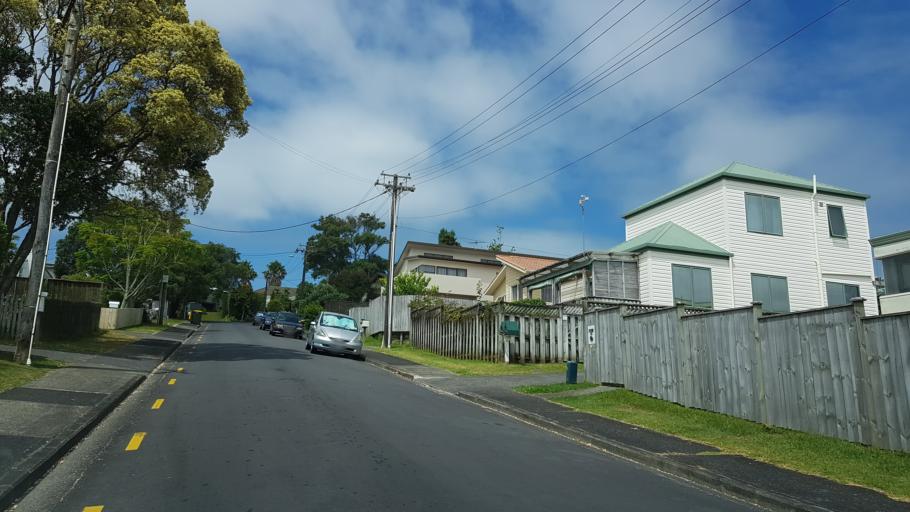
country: NZ
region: Auckland
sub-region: Auckland
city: North Shore
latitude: -36.7728
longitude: 174.7179
